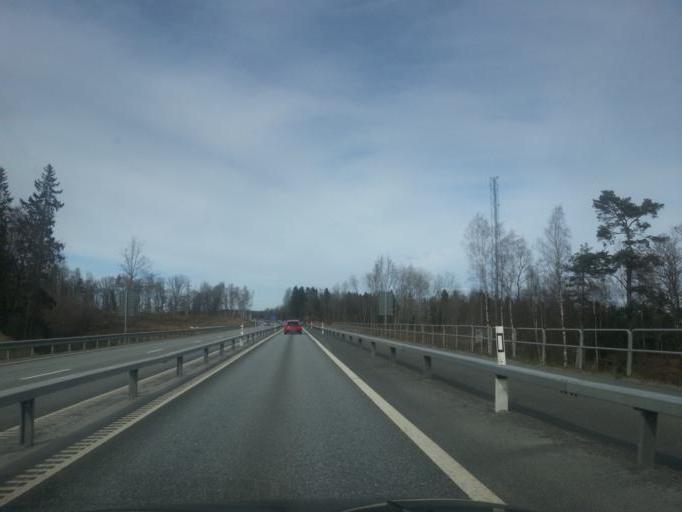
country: SE
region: Joenkoeping
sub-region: Habo Kommun
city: Habo
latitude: 57.8915
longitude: 14.1046
